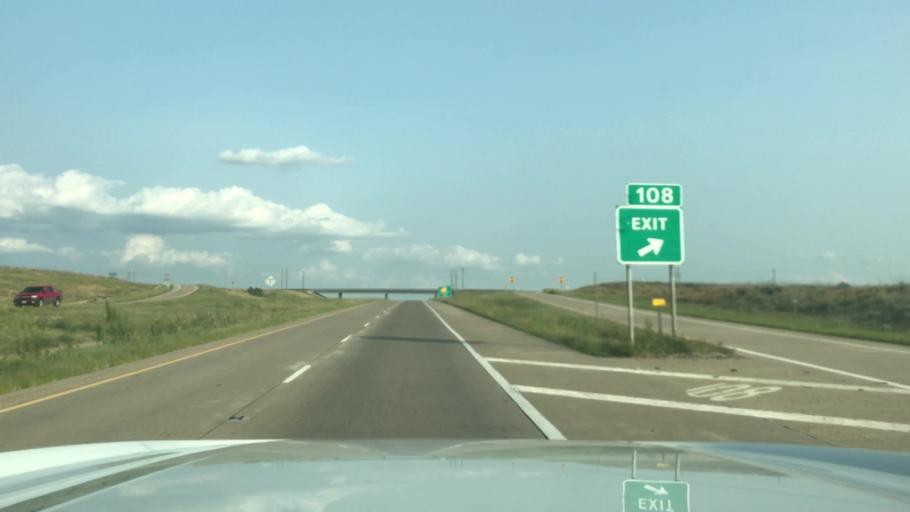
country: US
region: Texas
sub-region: Randall County
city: Canyon
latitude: 35.0029
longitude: -101.9005
